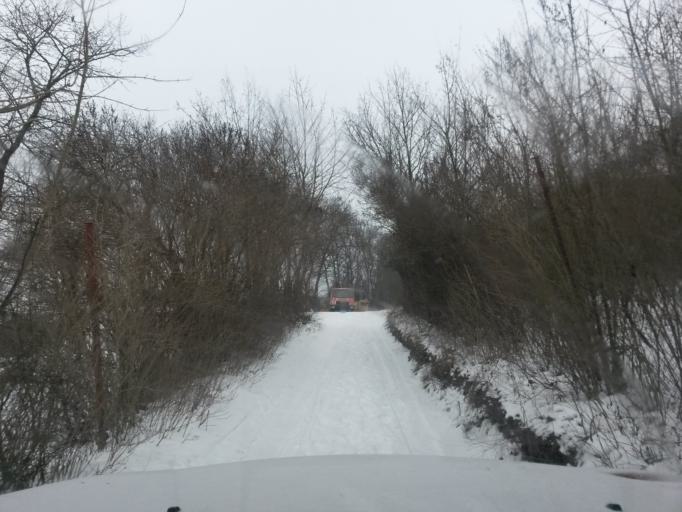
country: SK
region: Kosicky
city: Kosice
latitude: 48.8486
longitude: 21.2316
